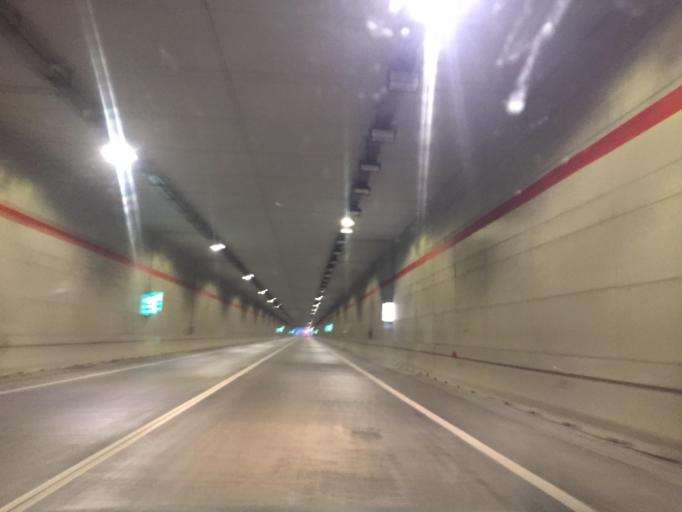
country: IT
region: Friuli Venezia Giulia
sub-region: Provincia di Udine
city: Dignano
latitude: 46.0797
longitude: 12.9349
